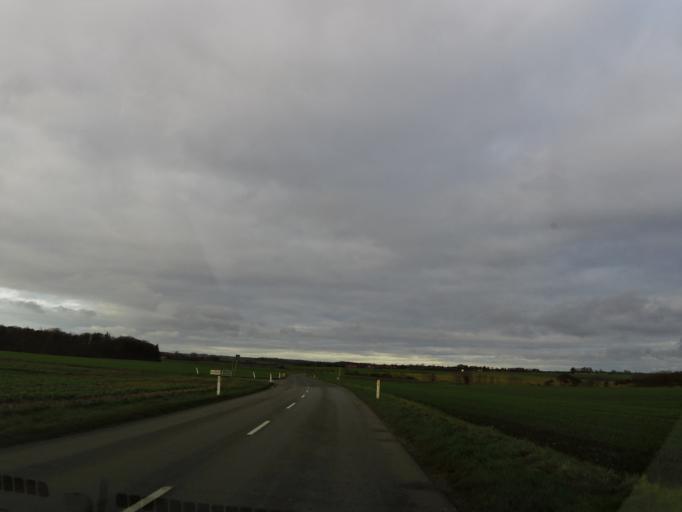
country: DK
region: Central Jutland
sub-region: Odder Kommune
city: Odder
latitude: 55.9580
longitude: 10.2361
